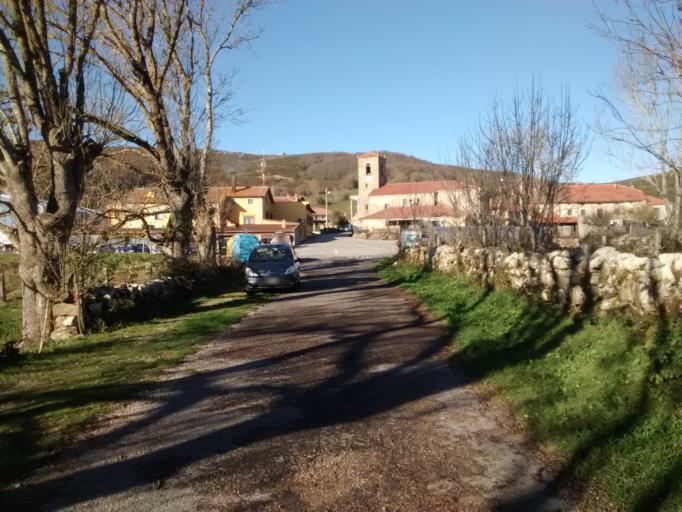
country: ES
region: Castille and Leon
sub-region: Provincia de Burgos
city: Arija
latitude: 43.0381
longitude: -3.8940
